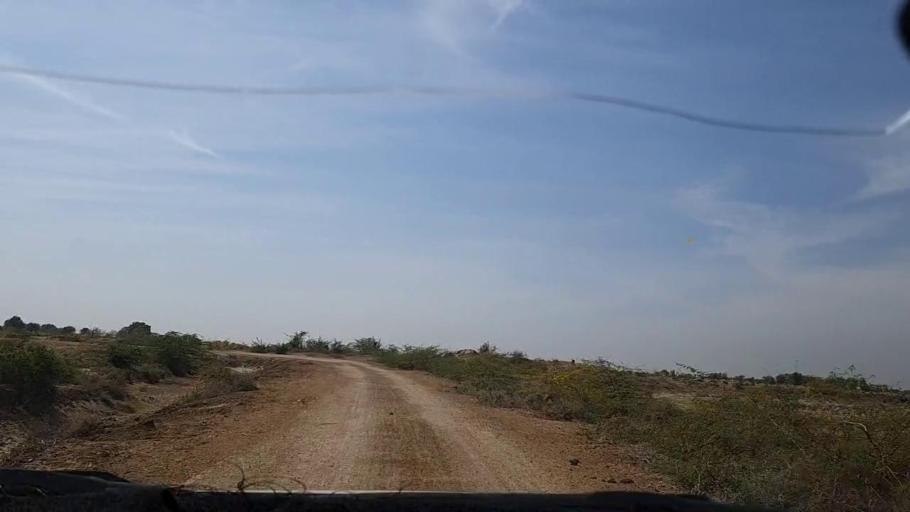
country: PK
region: Sindh
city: Pithoro
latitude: 25.4827
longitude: 69.4371
